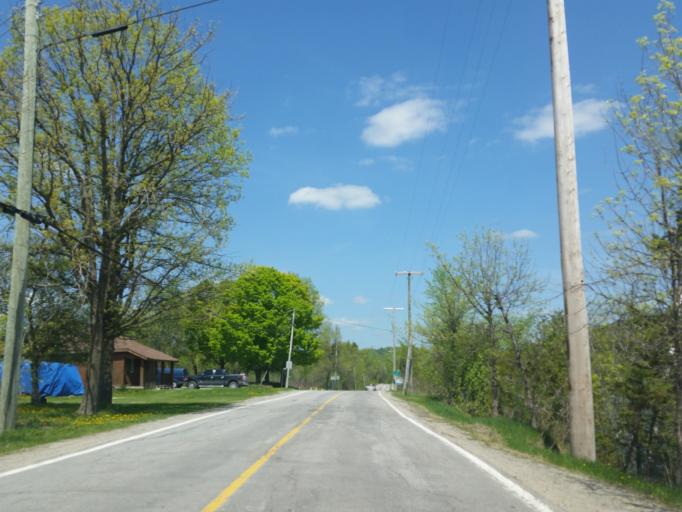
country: CA
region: Quebec
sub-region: Outaouais
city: Wakefield
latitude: 45.6151
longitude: -75.8985
